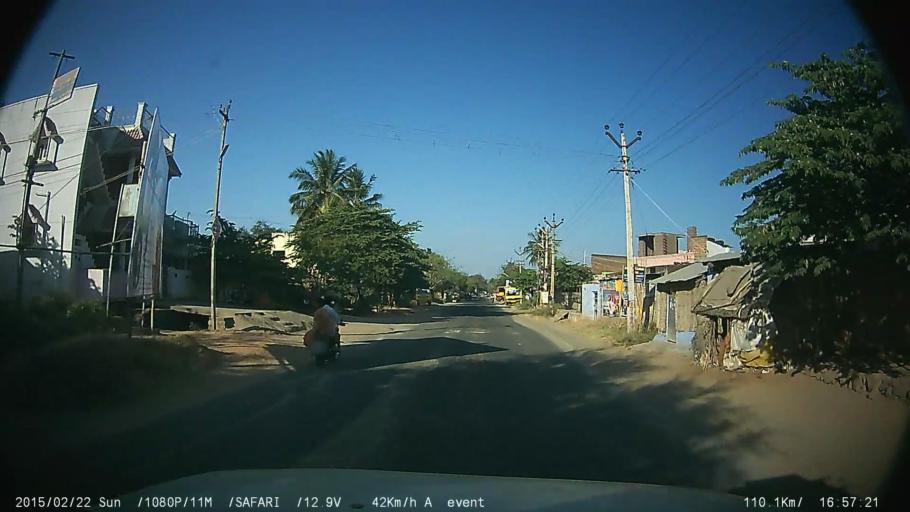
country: IN
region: Tamil Nadu
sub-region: Theni
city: Gudalur
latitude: 9.6827
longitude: 77.2459
